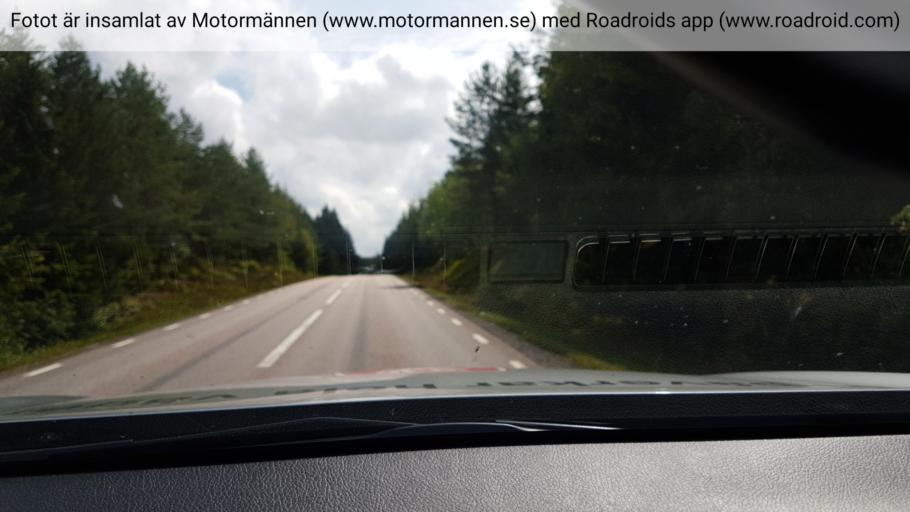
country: SE
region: Vaestra Goetaland
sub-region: Marks Kommun
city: Fritsla
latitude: 57.4954
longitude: 12.9396
